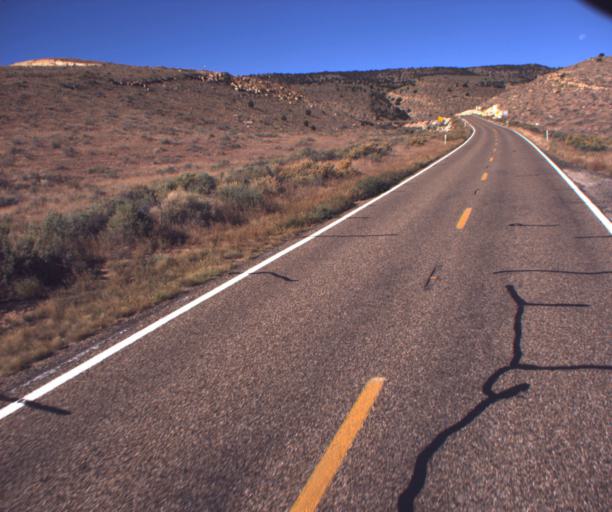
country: US
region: Arizona
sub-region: Coconino County
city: Fredonia
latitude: 36.7335
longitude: -112.0564
